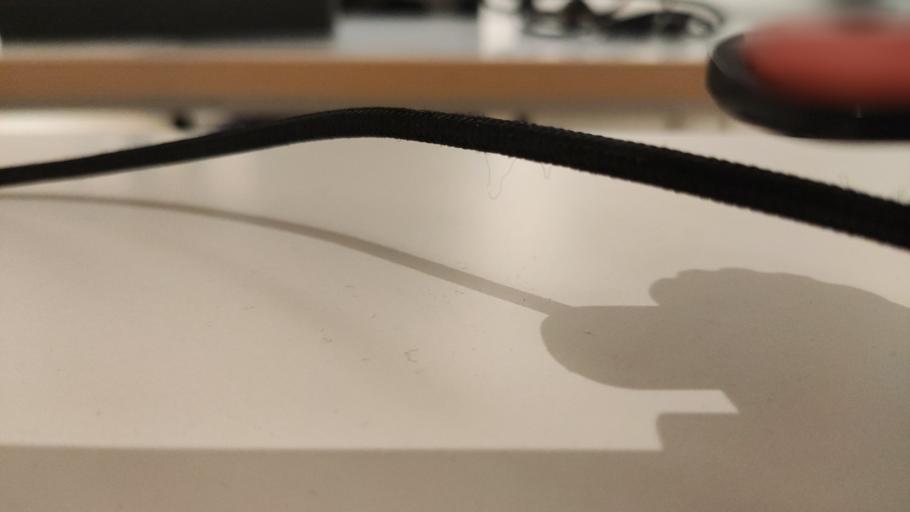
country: RU
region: Moskovskaya
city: Dorokhovo
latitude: 55.4185
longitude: 36.3640
